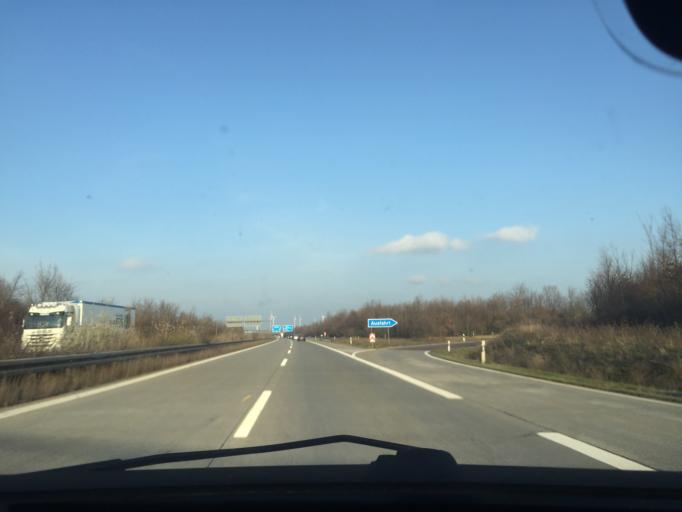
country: DE
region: Saxony-Anhalt
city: Diesdorf
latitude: 52.1443
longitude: 11.5419
